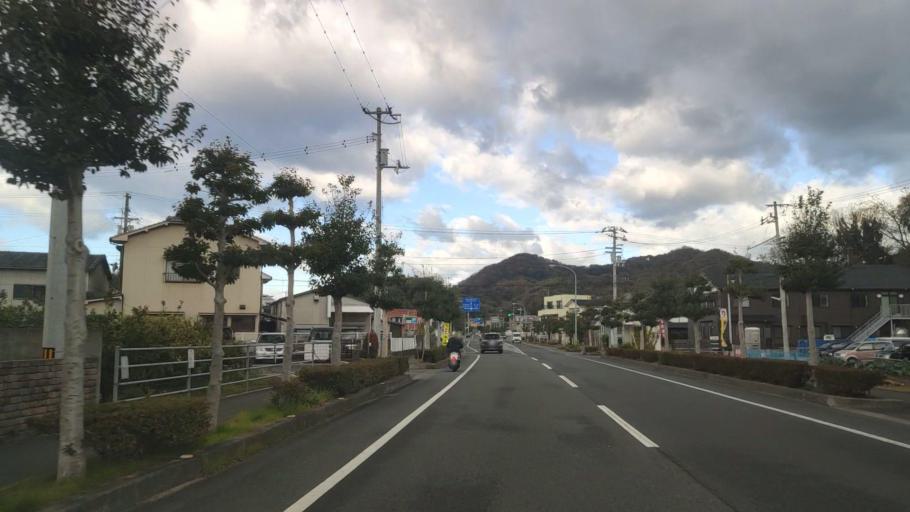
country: JP
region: Ehime
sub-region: Shikoku-chuo Shi
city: Matsuyama
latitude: 33.8709
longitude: 132.7212
